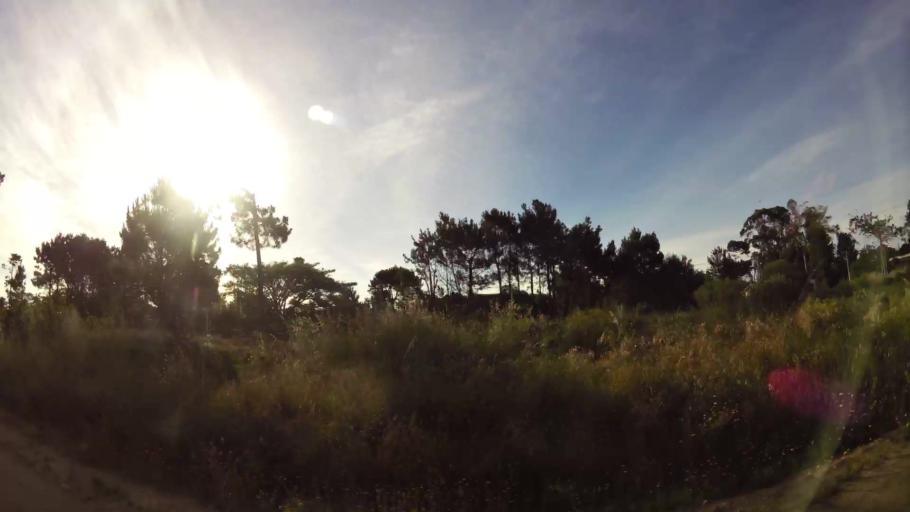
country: UY
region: Canelones
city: Empalme Olmos
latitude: -34.7847
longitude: -55.8556
